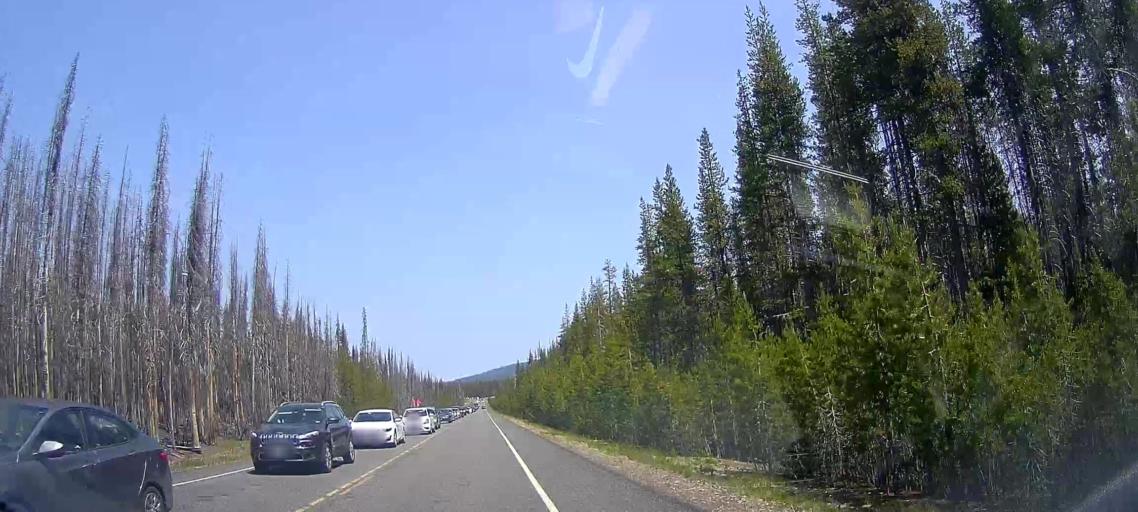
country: US
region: Oregon
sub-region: Lane County
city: Oakridge
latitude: 43.0796
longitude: -122.1177
